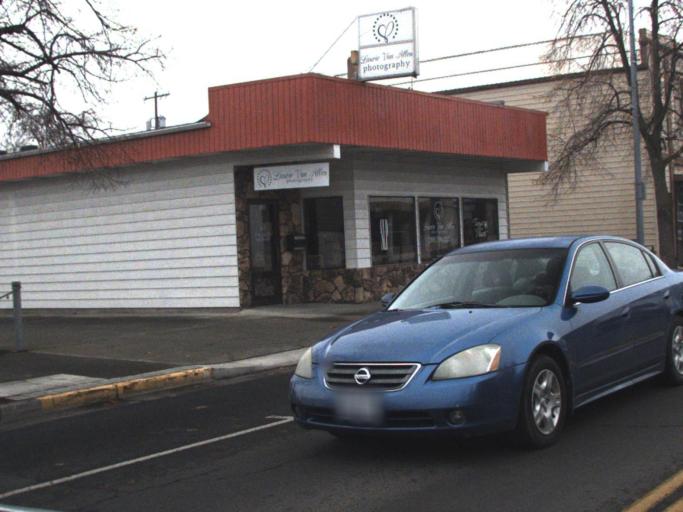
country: US
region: Washington
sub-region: Asotin County
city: Clarkston
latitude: 46.4117
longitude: -117.0456
